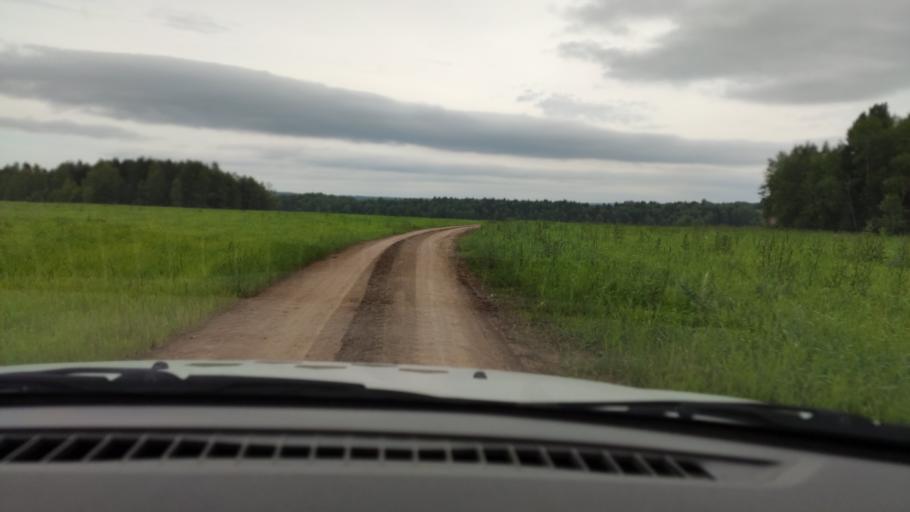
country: RU
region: Perm
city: Orda
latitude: 57.2964
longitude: 56.5935
